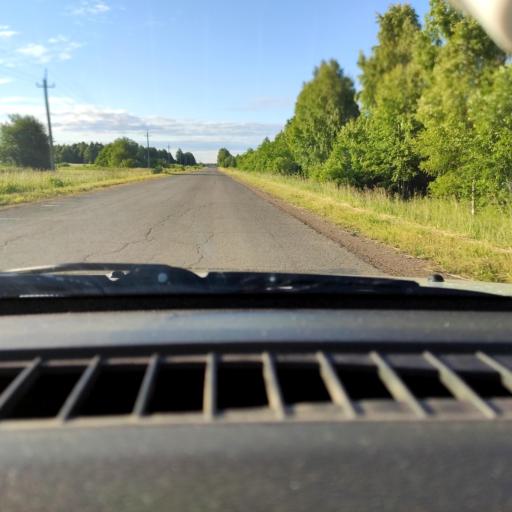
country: RU
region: Perm
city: Uinskoye
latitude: 57.0968
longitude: 56.5470
